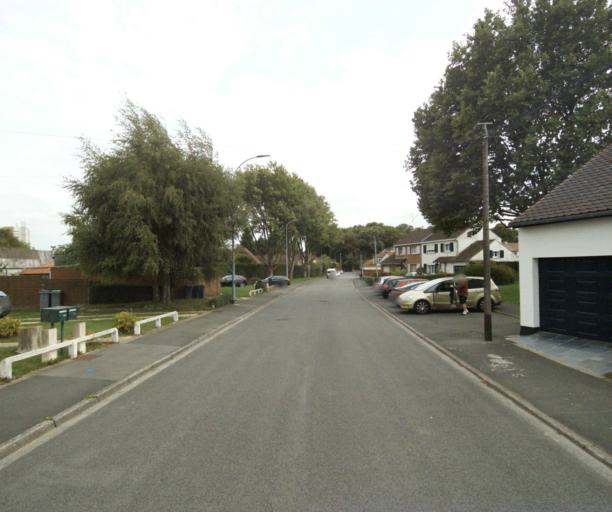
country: FR
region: Nord-Pas-de-Calais
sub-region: Departement du Nord
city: Lambersart
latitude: 50.6578
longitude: 3.0236
